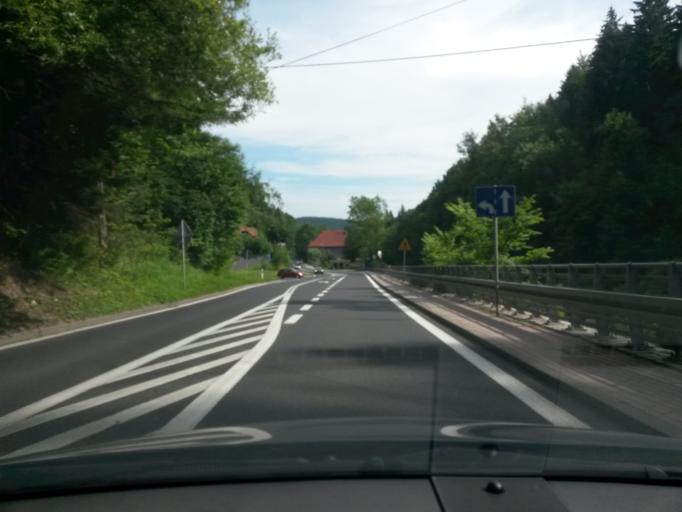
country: PL
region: Lower Silesian Voivodeship
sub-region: Powiat jeleniogorski
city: Piechowice
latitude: 50.8416
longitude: 15.5672
